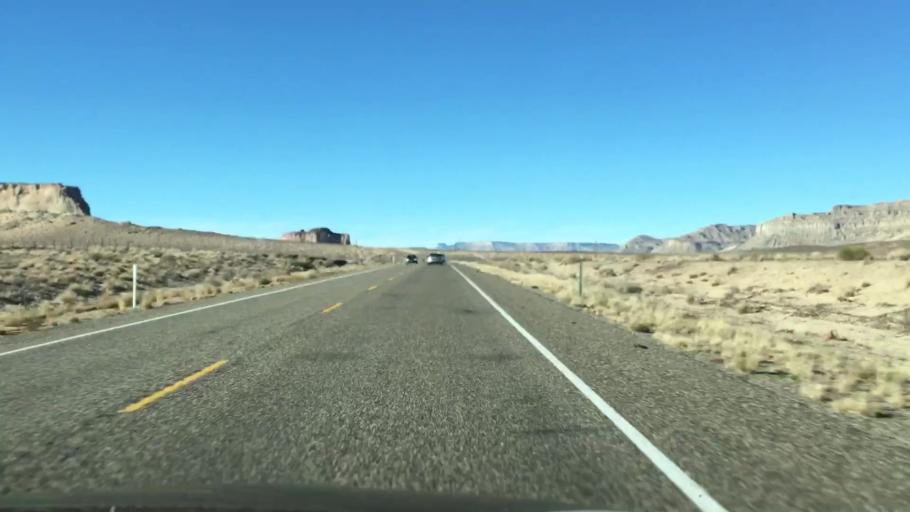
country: US
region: Arizona
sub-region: Coconino County
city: Page
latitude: 37.0242
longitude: -111.5980
